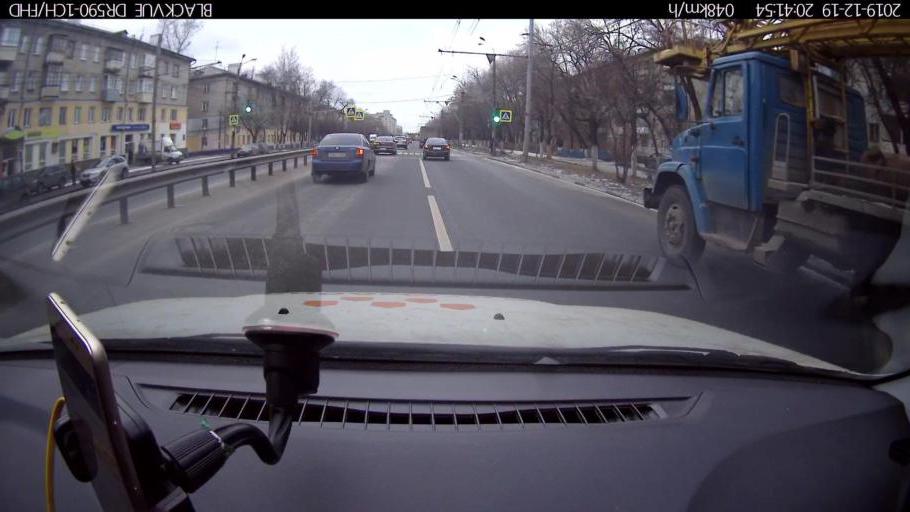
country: RU
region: Nizjnij Novgorod
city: Nizhniy Novgorod
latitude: 56.3202
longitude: 43.8883
